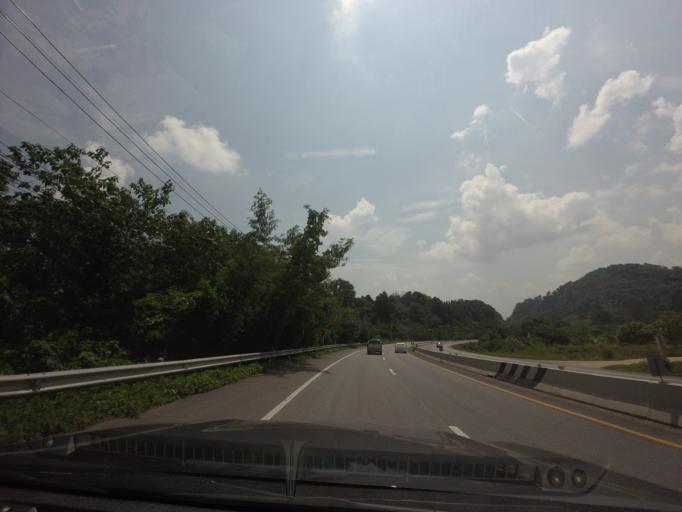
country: TH
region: Uttaradit
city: Lap Lae
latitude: 17.7751
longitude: 100.1310
